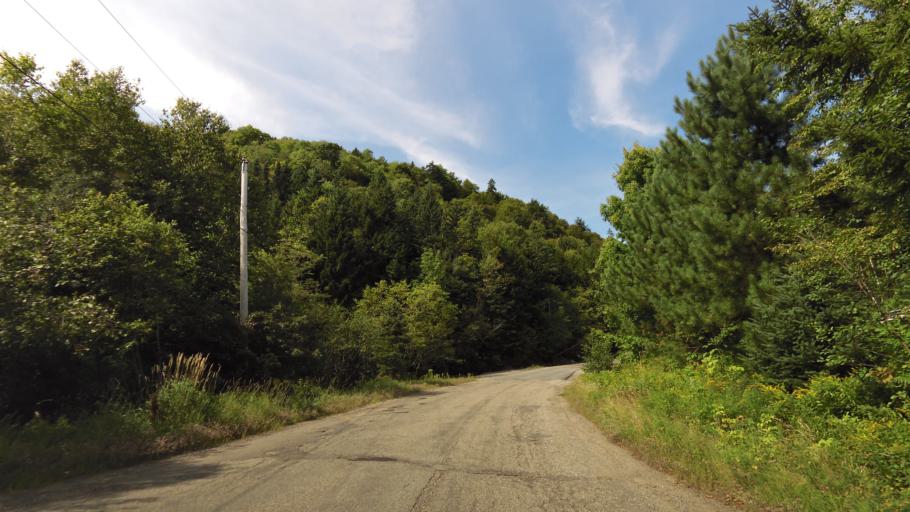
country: CA
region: New Brunswick
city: Hampton
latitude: 45.5498
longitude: -65.8376
